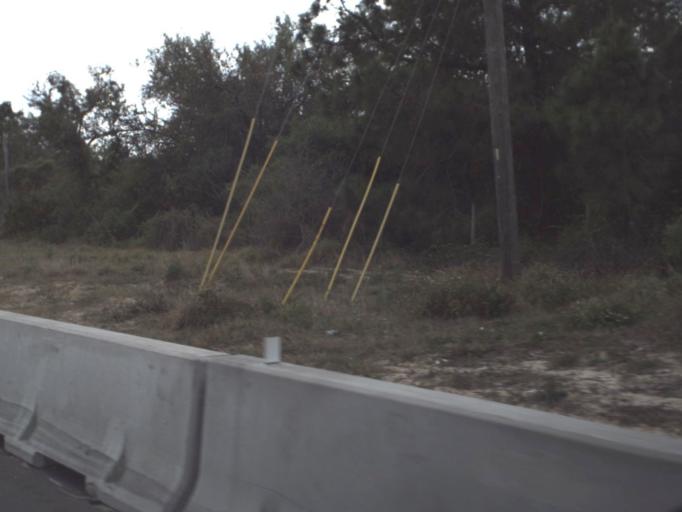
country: US
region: Florida
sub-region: Lake County
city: Clermont
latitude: 28.4742
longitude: -81.7157
